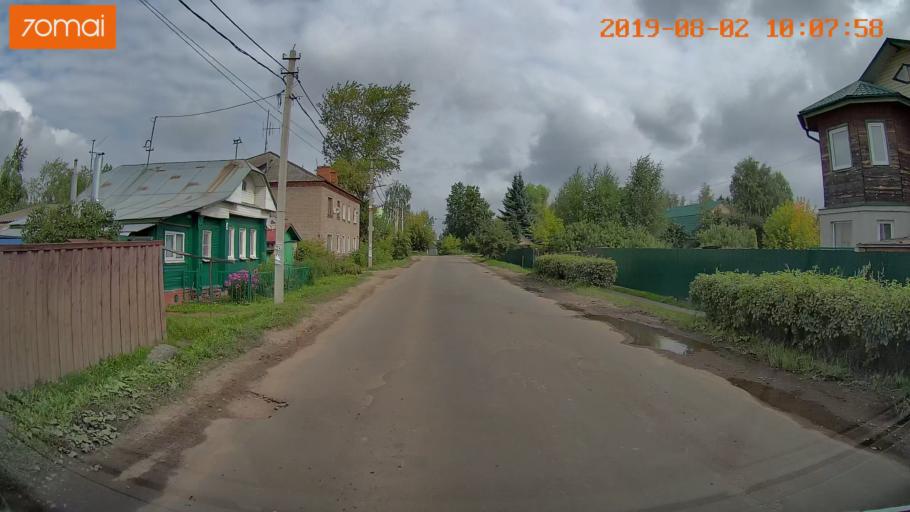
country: RU
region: Ivanovo
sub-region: Gorod Ivanovo
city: Ivanovo
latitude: 56.9846
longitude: 40.9367
